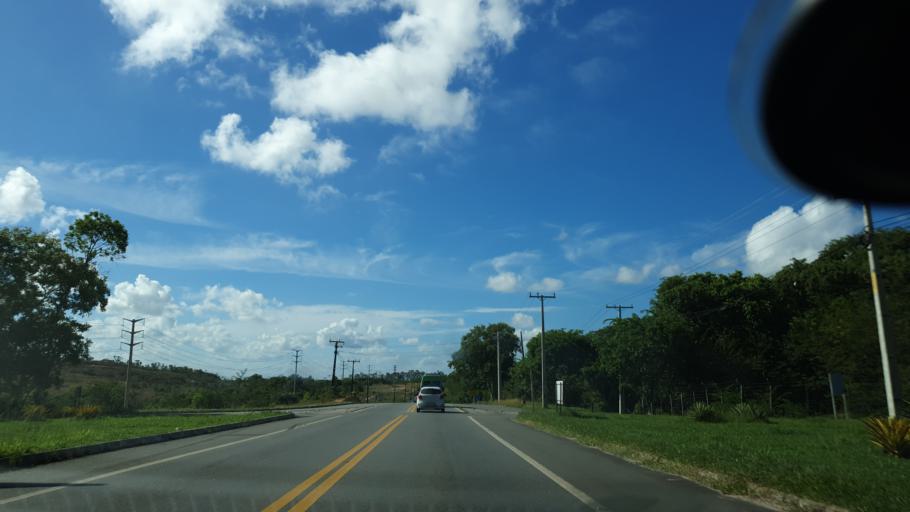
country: BR
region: Bahia
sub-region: Camacari
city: Camacari
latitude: -12.6897
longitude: -38.2269
